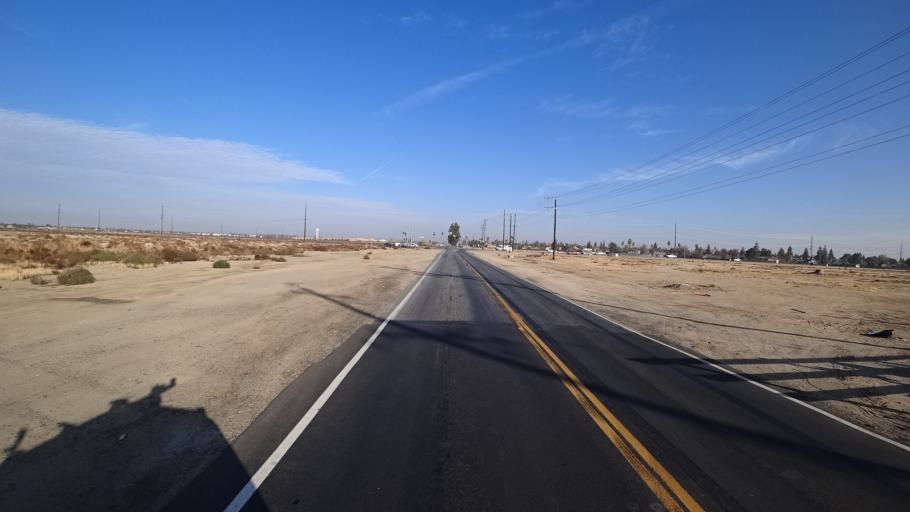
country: US
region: California
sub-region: Kern County
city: Greenacres
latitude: 35.2943
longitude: -119.0922
